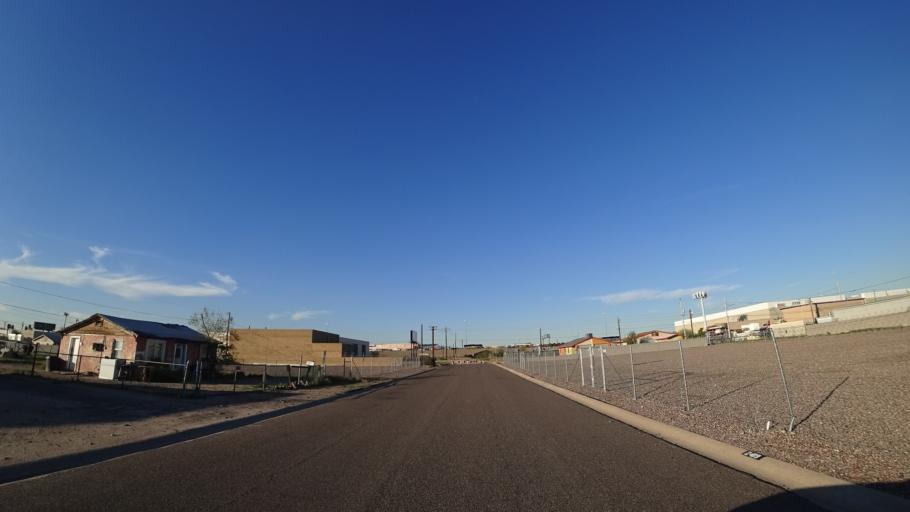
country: US
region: Arizona
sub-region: Maricopa County
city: Phoenix
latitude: 33.4249
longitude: -112.0435
